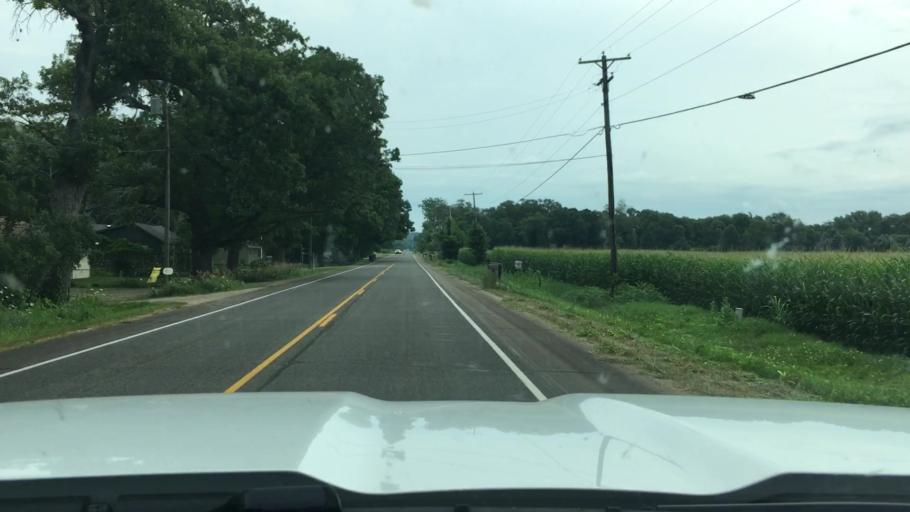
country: US
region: Michigan
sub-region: Allegan County
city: Plainwell
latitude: 42.4646
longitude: -85.6312
